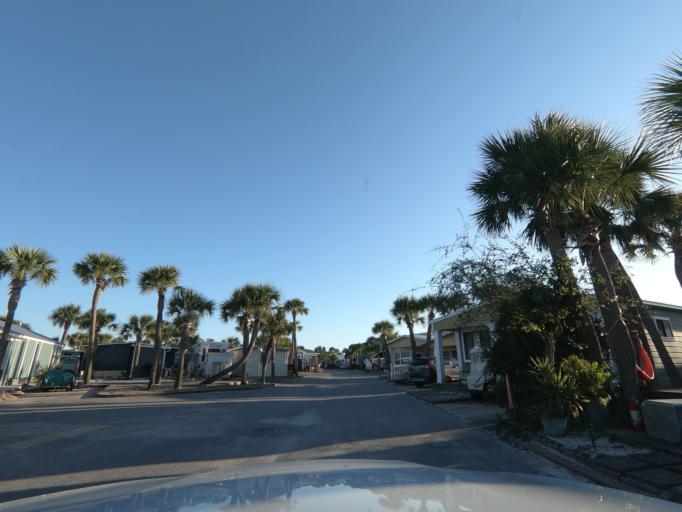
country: US
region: Florida
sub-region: Bay County
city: Lower Grand Lagoon
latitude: 30.1404
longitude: -85.7480
